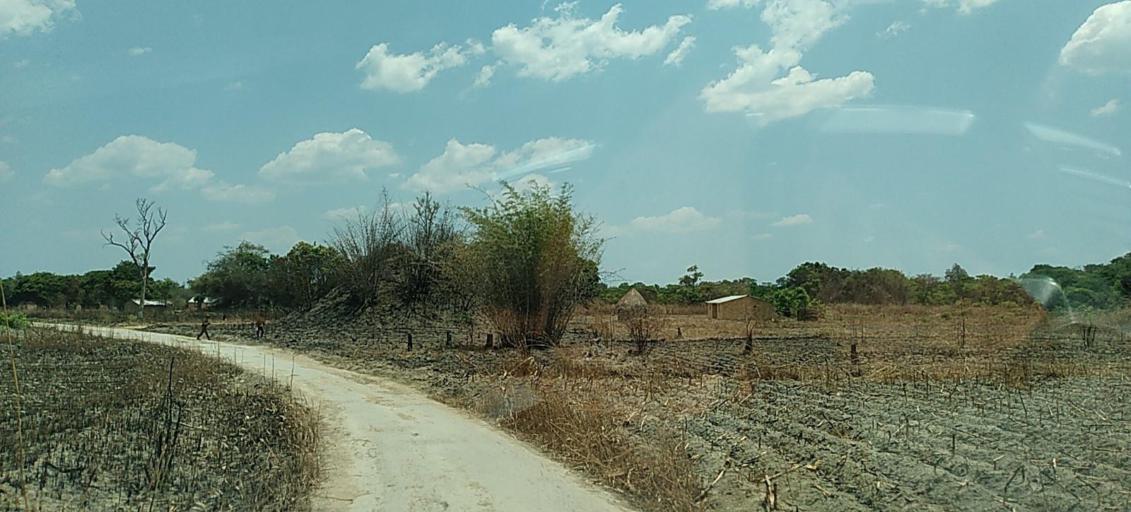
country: ZM
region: Copperbelt
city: Chililabombwe
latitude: -12.4840
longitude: 27.6699
